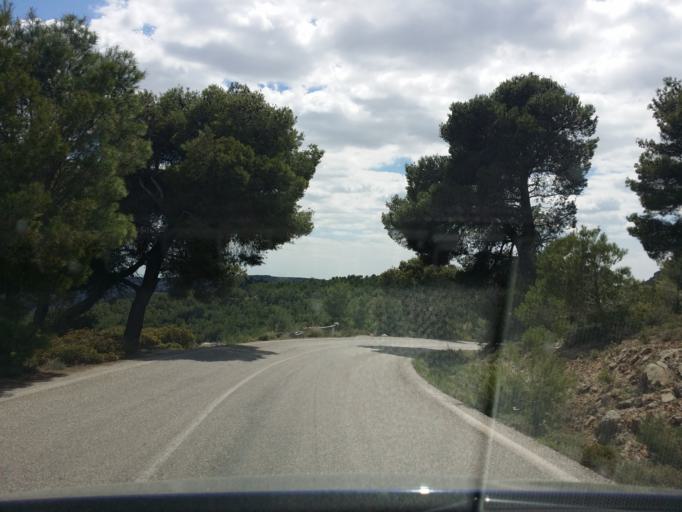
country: GR
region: Attica
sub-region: Nomarchia Dytikis Attikis
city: Fyli
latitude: 38.1287
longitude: 23.6471
